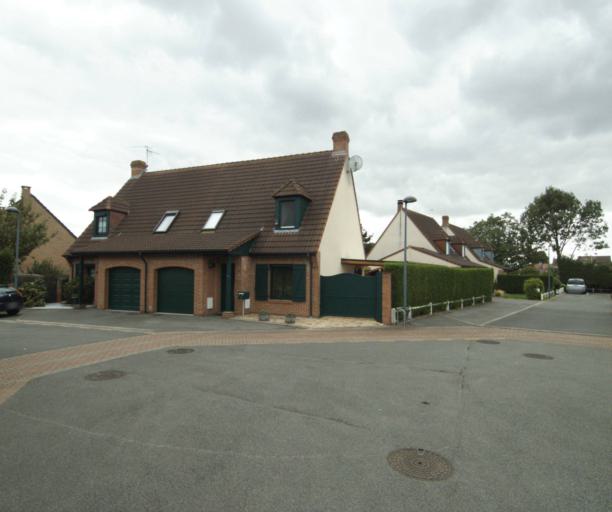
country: FR
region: Nord-Pas-de-Calais
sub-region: Departement du Nord
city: Saint-Andre-lez-Lille
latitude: 50.6666
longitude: 3.0334
